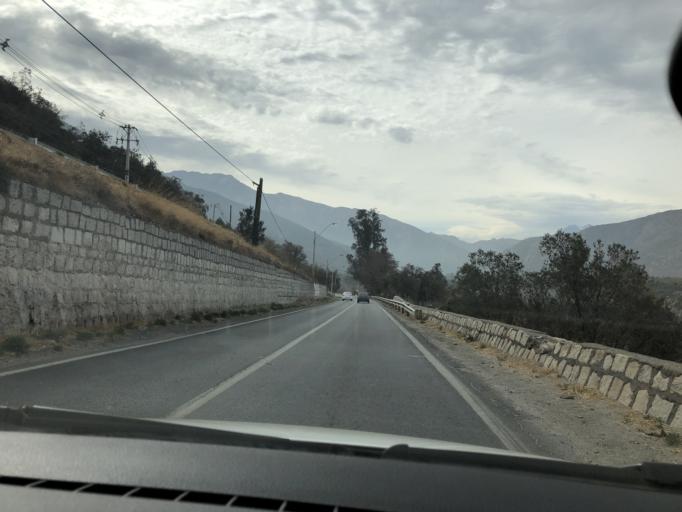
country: CL
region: Santiago Metropolitan
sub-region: Provincia de Cordillera
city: Puente Alto
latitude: -33.5970
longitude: -70.4935
